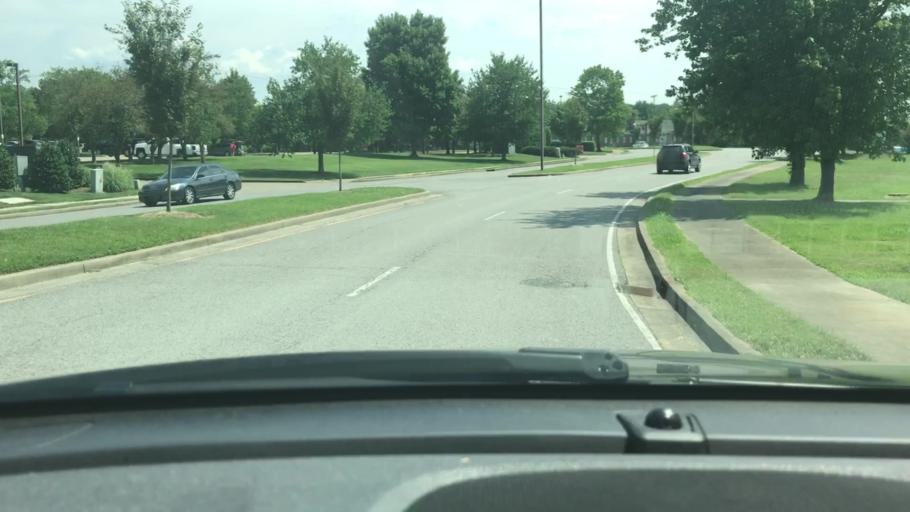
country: US
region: Tennessee
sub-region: Sumner County
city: Hendersonville
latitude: 36.3134
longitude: -86.5978
